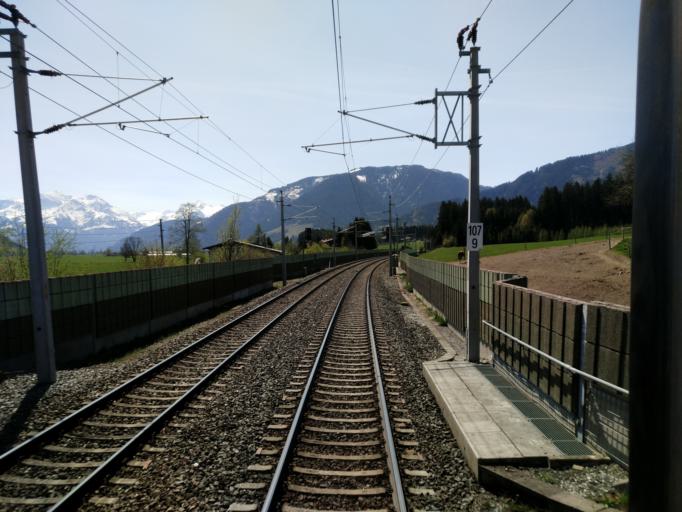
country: AT
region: Salzburg
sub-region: Politischer Bezirk Zell am See
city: Maishofen
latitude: 47.3898
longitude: 12.8267
